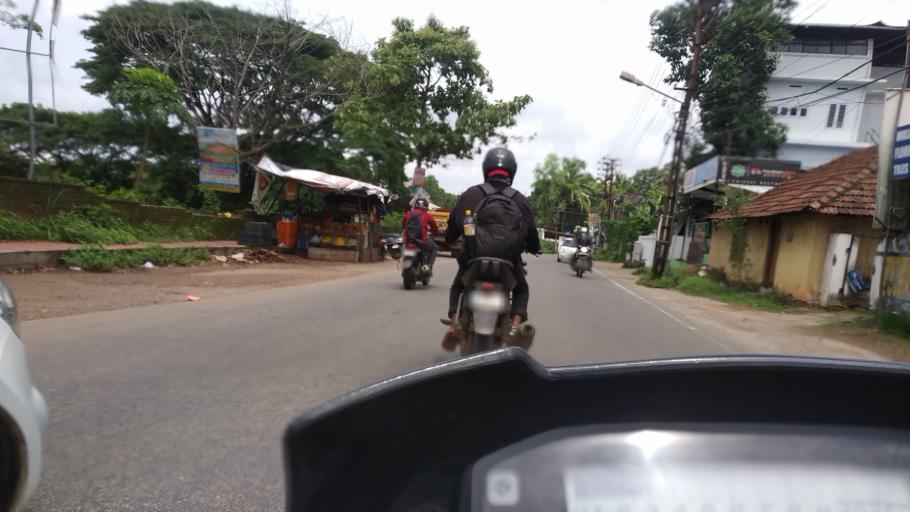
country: IN
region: Kerala
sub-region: Ernakulam
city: Aluva
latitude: 10.1226
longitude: 76.3357
